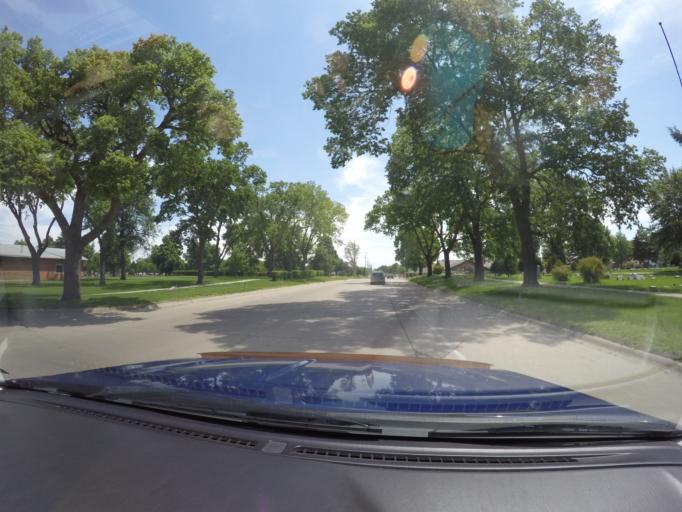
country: US
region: Nebraska
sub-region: Hall County
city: Grand Island
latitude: 40.9025
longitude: -98.3744
